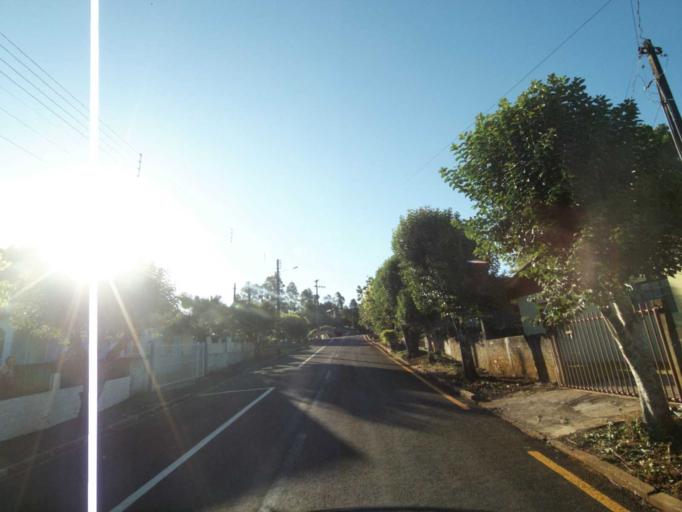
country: BR
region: Parana
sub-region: Coronel Vivida
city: Coronel Vivida
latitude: -25.9743
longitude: -52.8169
